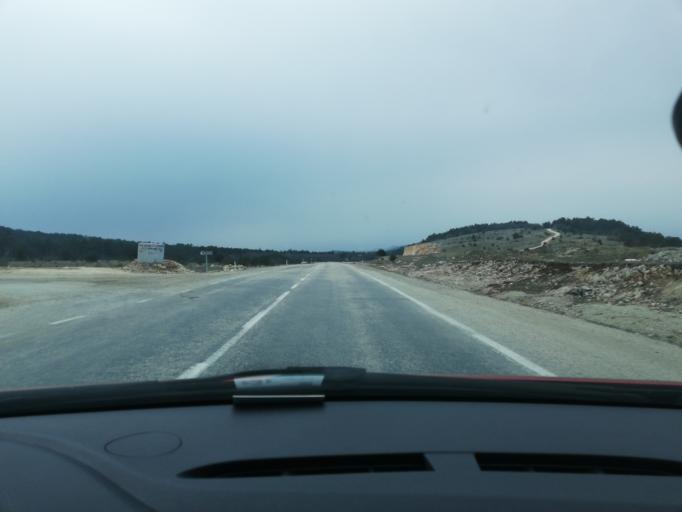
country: TR
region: Kastamonu
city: Pinarbasi
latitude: 41.5591
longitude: 33.0803
